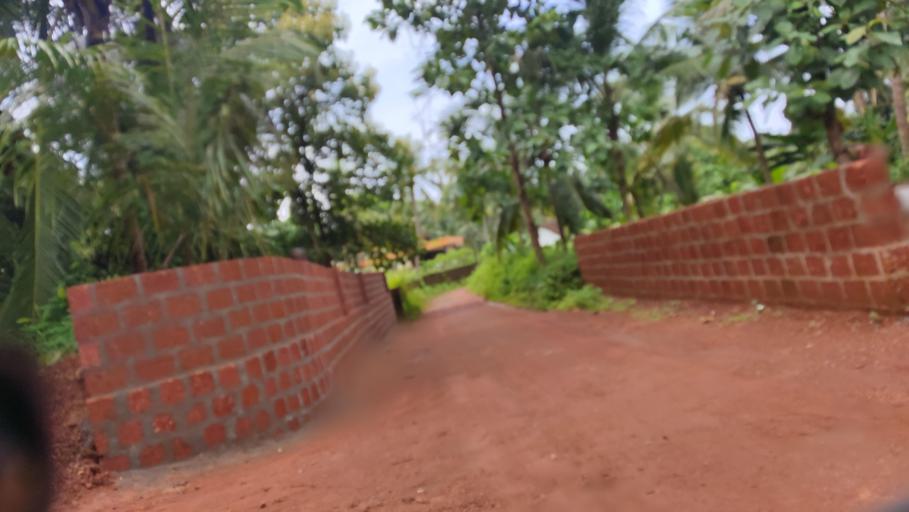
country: IN
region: Kerala
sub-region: Kasaragod District
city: Kannangad
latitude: 12.3979
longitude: 75.0558
